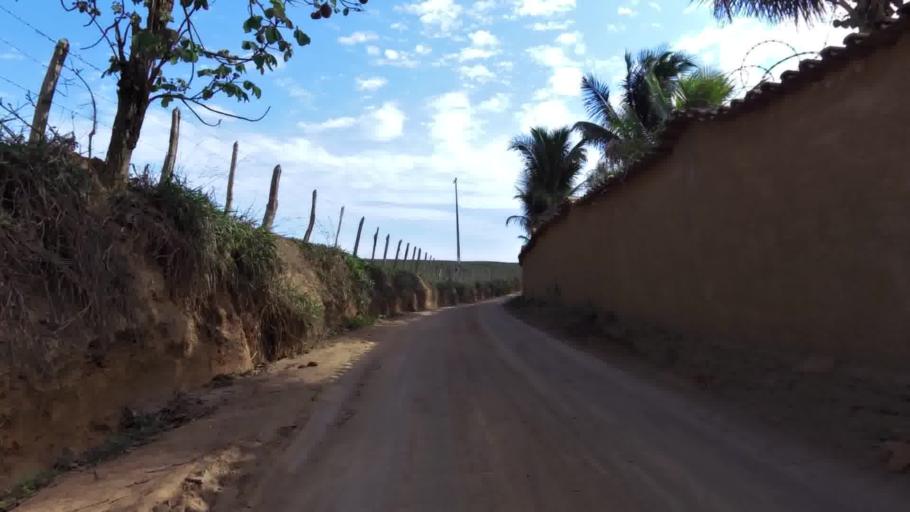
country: BR
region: Espirito Santo
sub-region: Piuma
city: Piuma
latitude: -20.8215
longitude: -40.7434
